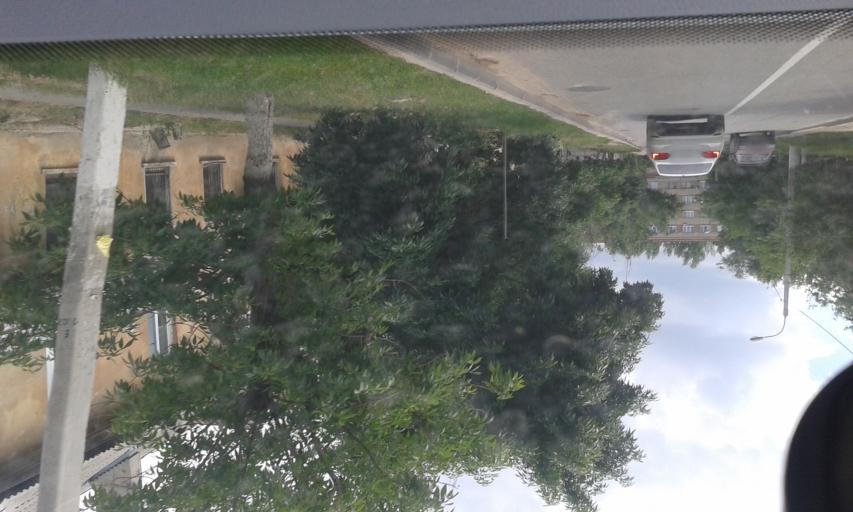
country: RU
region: Volgograd
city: Gorodishche
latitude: 48.7721
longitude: 44.4798
